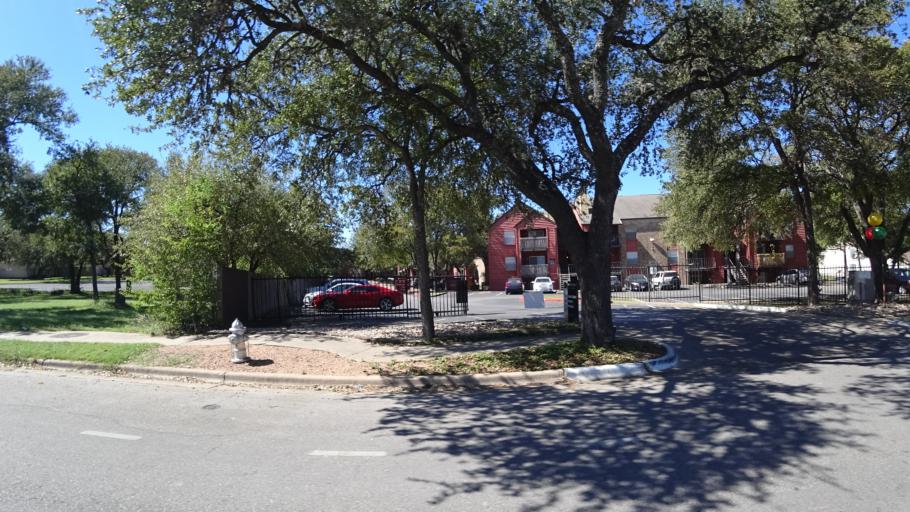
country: US
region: Texas
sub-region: Travis County
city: Austin
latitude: 30.2245
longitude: -97.7423
